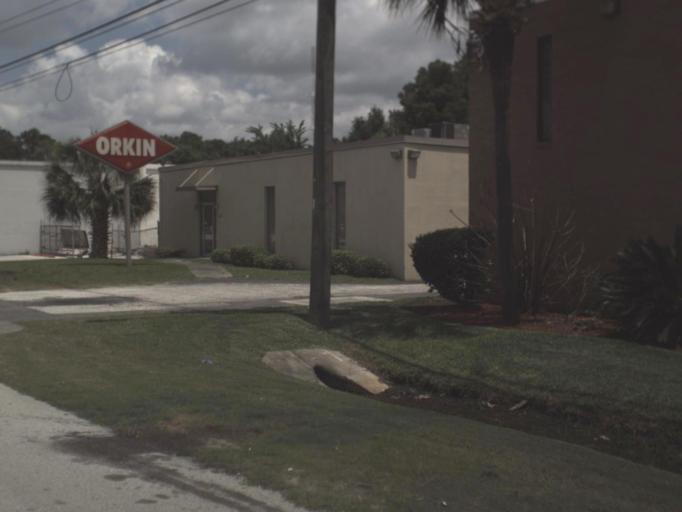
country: US
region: Florida
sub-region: Duval County
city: Jacksonville
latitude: 30.2591
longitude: -81.6127
